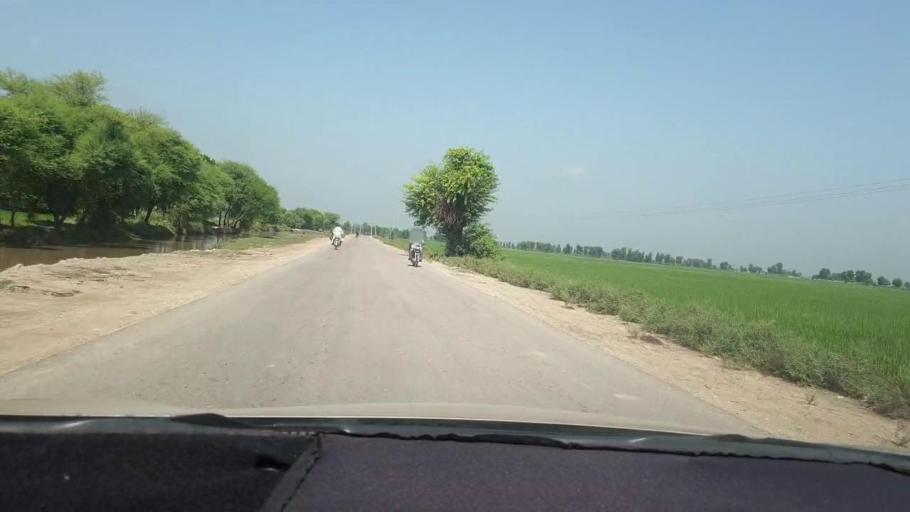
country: PK
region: Sindh
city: Miro Khan
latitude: 27.7657
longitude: 68.0720
